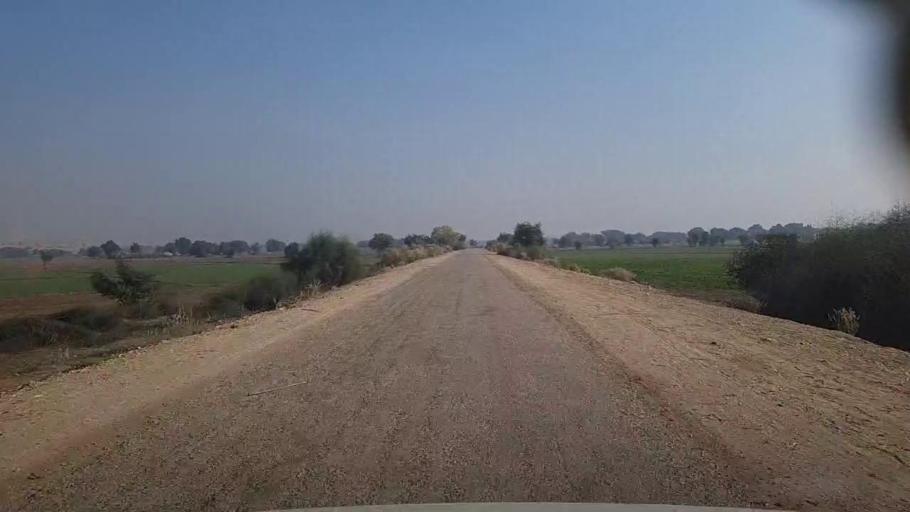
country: PK
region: Sindh
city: Kandiari
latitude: 26.8207
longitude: 68.4924
